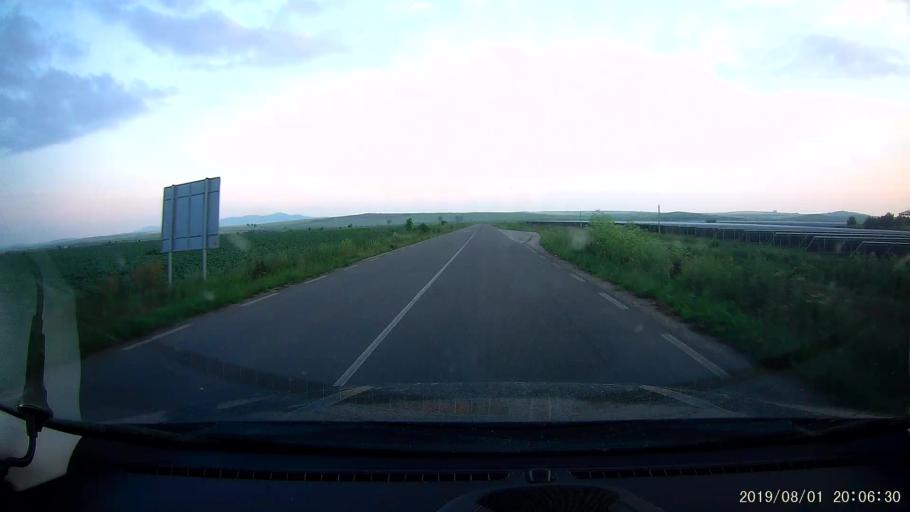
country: BG
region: Yambol
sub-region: Obshtina Yambol
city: Yambol
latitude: 42.5343
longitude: 26.5560
